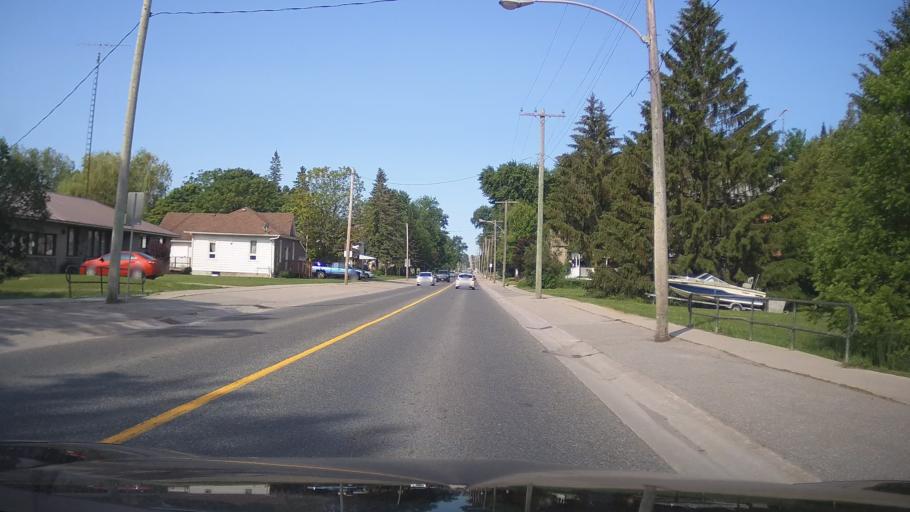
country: CA
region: Ontario
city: Omemee
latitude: 44.2983
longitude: -78.5625
